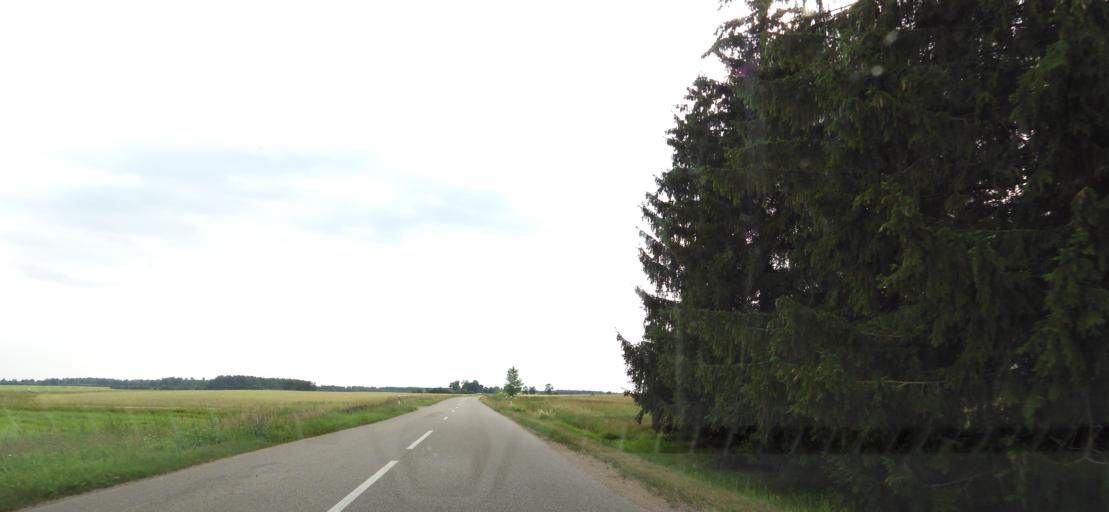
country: LT
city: Obeliai
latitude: 56.1427
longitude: 25.1349
